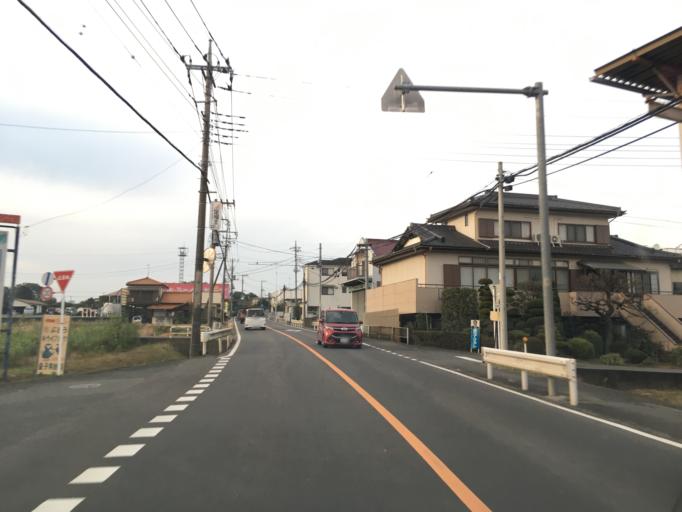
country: JP
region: Saitama
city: Sayama
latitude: 35.8808
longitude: 139.3781
